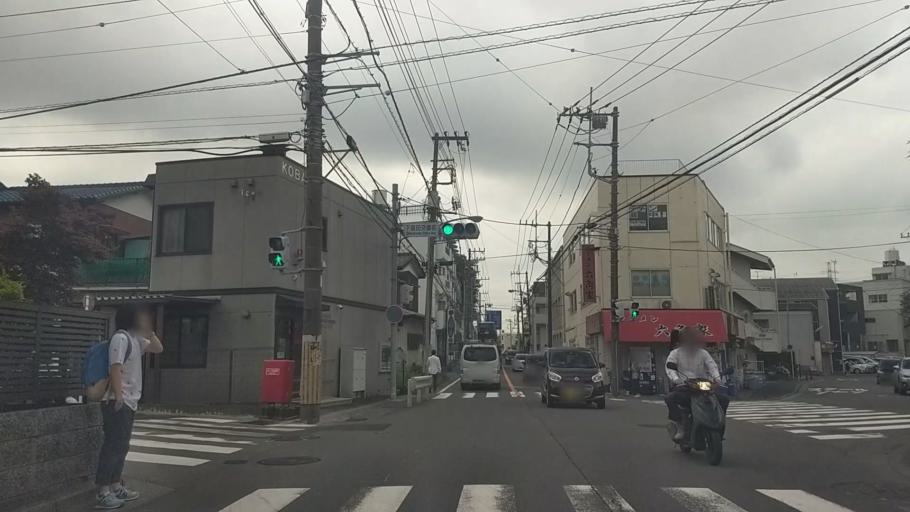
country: JP
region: Kanagawa
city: Kamakura
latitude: 35.3840
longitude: 139.5363
